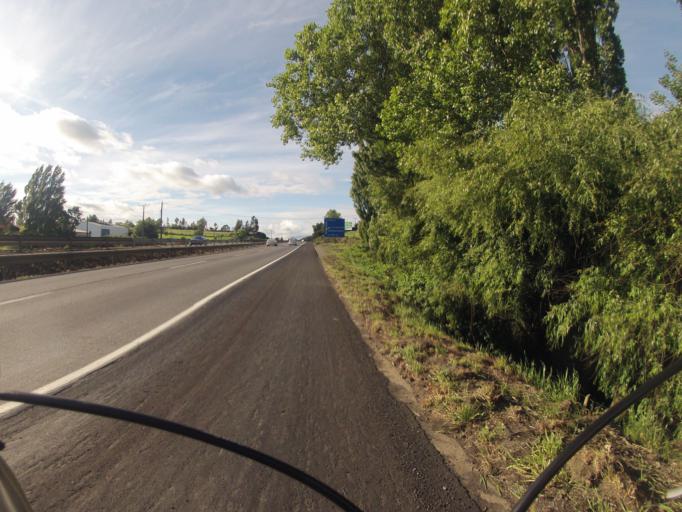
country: CL
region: Araucania
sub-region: Provincia de Cautin
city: Temuco
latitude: -38.8154
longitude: -72.6244
